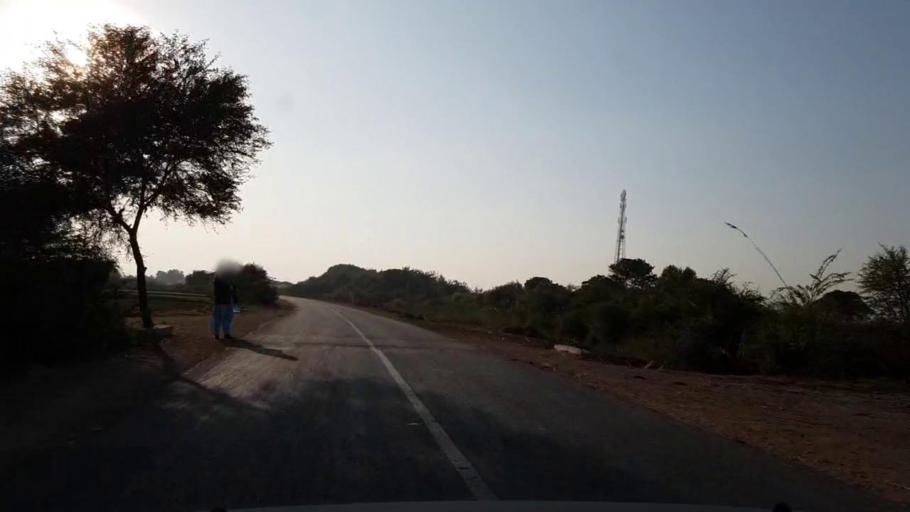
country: PK
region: Sindh
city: Mirpur Batoro
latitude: 24.6862
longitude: 68.1670
